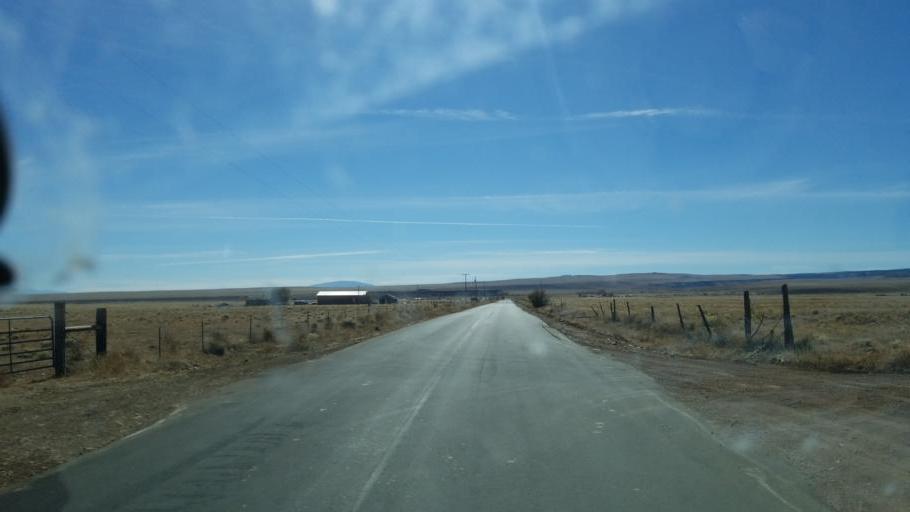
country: US
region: Colorado
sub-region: Conejos County
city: Conejos
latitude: 37.2981
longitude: -106.1478
